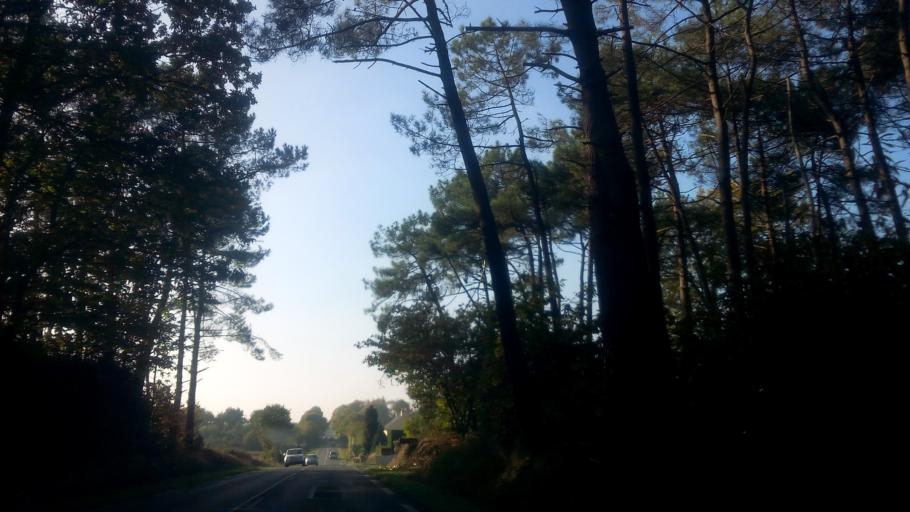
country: FR
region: Pays de la Loire
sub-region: Departement de la Loire-Atlantique
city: Avessac
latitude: 47.6407
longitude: -2.0161
